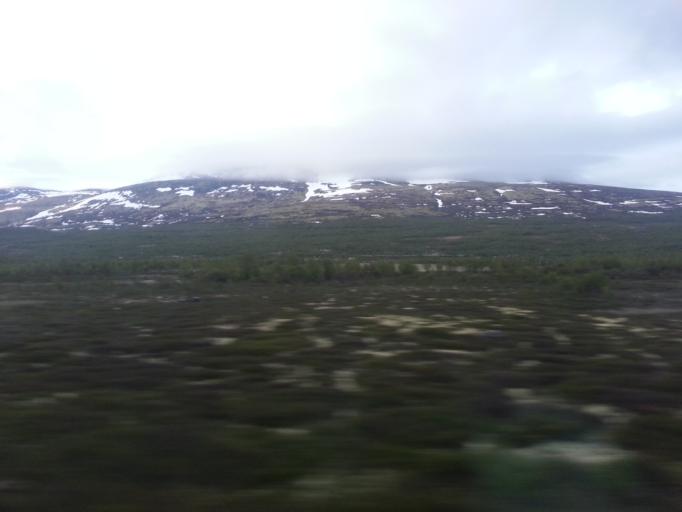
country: NO
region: Oppland
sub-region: Dovre
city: Dovre
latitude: 62.1471
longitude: 9.3157
